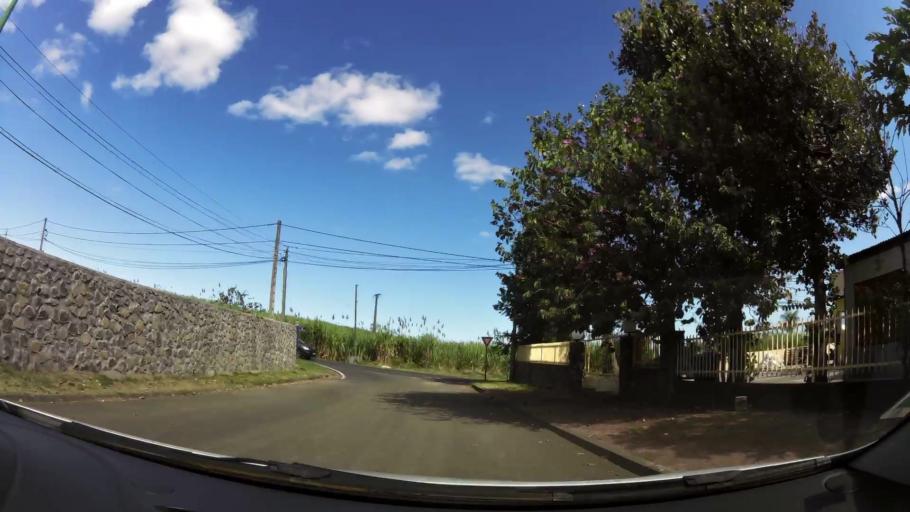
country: RE
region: Reunion
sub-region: Reunion
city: Le Tampon
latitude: -21.2814
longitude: 55.5020
